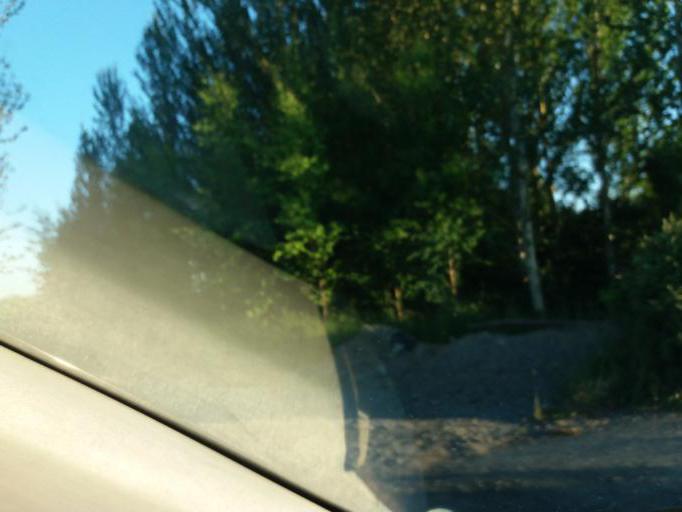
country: IE
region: Leinster
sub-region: Dublin City
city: Finglas
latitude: 53.4503
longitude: -6.3218
